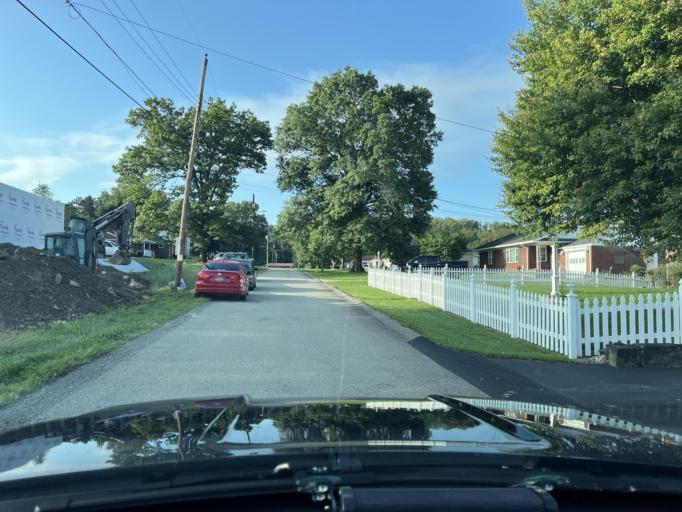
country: US
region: Pennsylvania
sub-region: Fayette County
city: Leith-Hatfield
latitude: 39.8866
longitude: -79.7276
